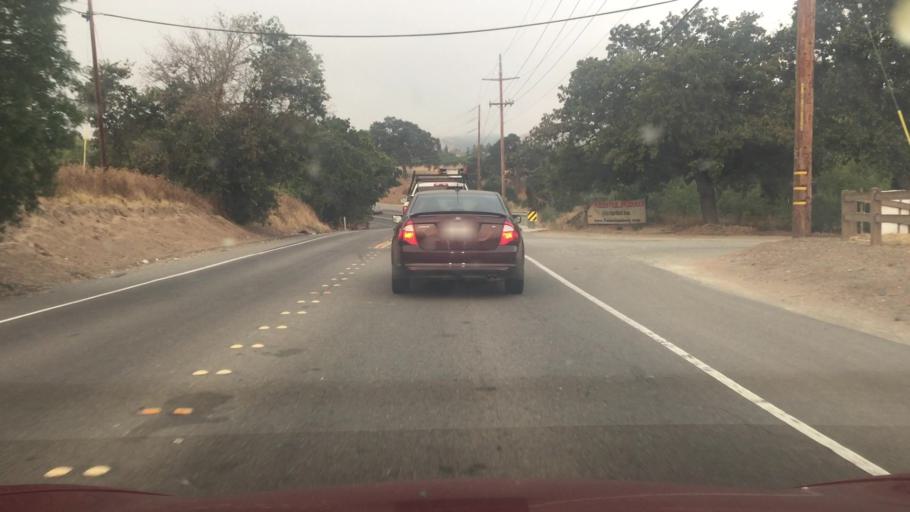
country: US
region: California
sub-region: Alameda County
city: Livermore
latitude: 37.6407
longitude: -121.7949
